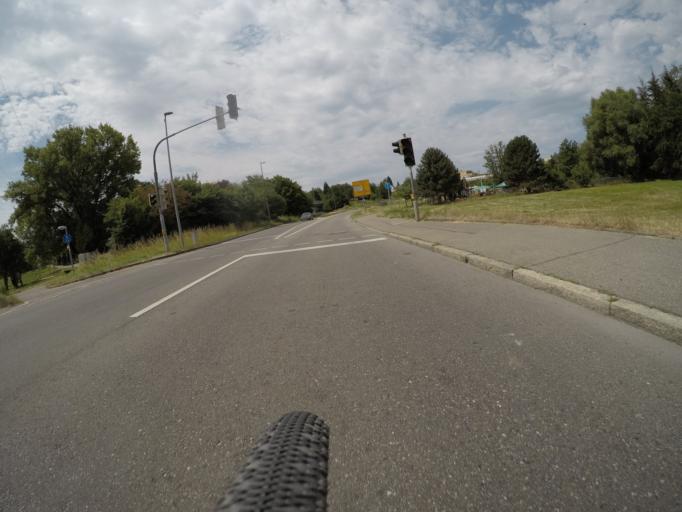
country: DE
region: Baden-Wuerttemberg
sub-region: Regierungsbezirk Stuttgart
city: Magstadt
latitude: 48.7273
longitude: 8.9826
